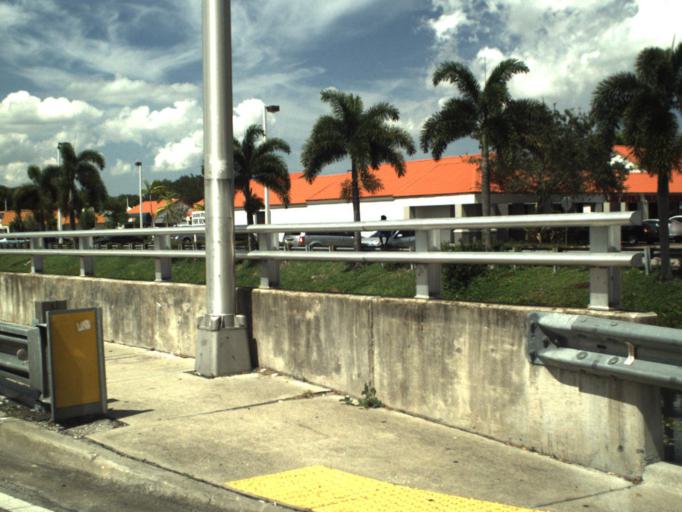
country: US
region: Florida
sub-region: Broward County
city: Pembroke Pines
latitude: 26.0104
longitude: -80.2480
